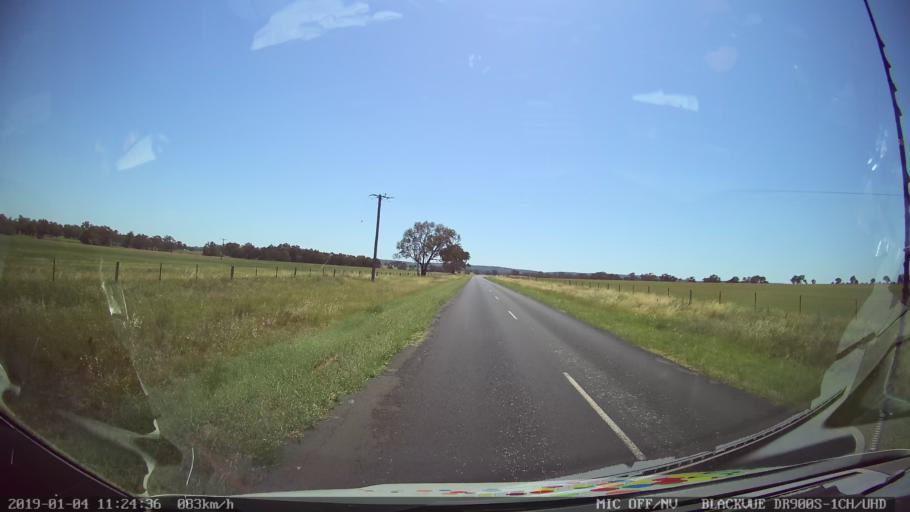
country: AU
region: New South Wales
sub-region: Cabonne
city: Molong
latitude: -33.1316
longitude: 148.7490
